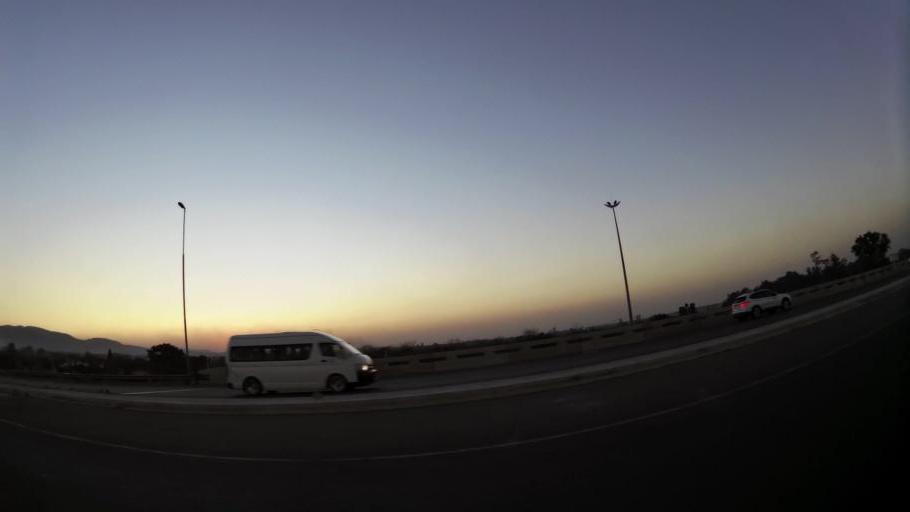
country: ZA
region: North-West
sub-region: Bojanala Platinum District Municipality
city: Rustenburg
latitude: -25.6474
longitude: 27.2554
